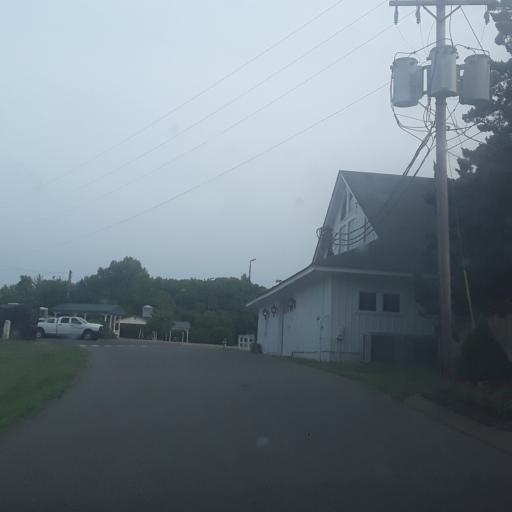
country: US
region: Tennessee
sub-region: Davidson County
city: Oak Hill
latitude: 36.0629
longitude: -86.7458
